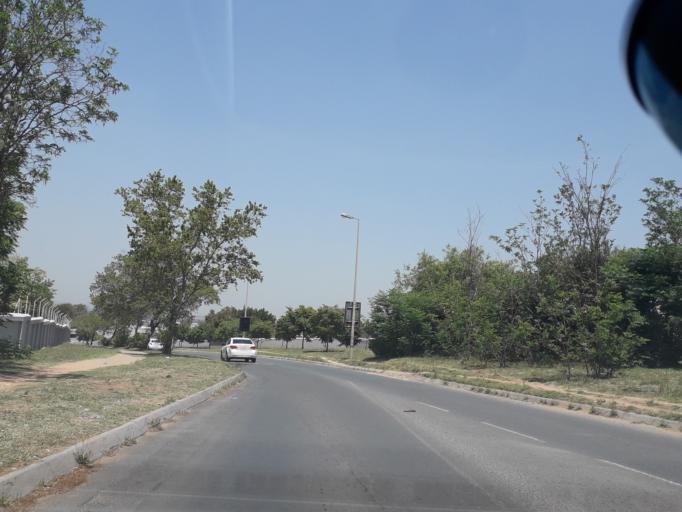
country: ZA
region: Gauteng
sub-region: City of Johannesburg Metropolitan Municipality
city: Midrand
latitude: -25.9957
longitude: 28.1045
